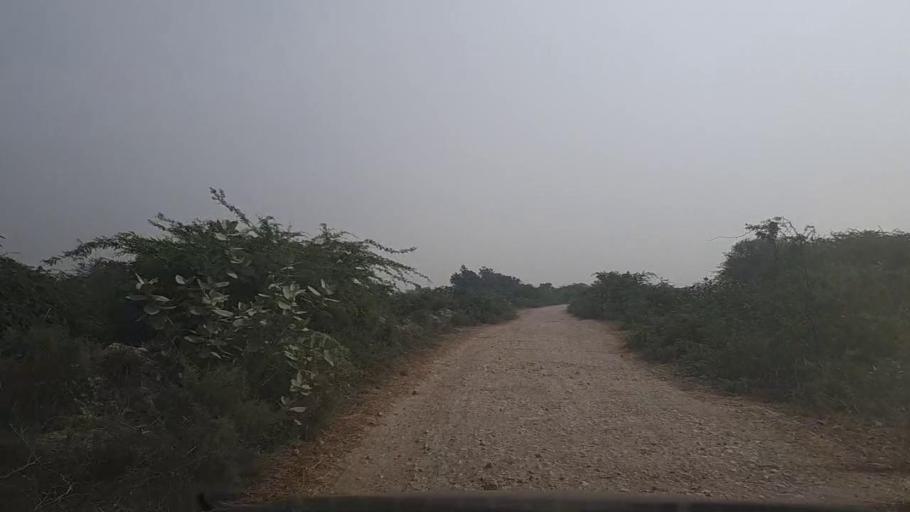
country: PK
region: Sindh
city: Mirpur Sakro
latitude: 24.4845
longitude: 67.6437
